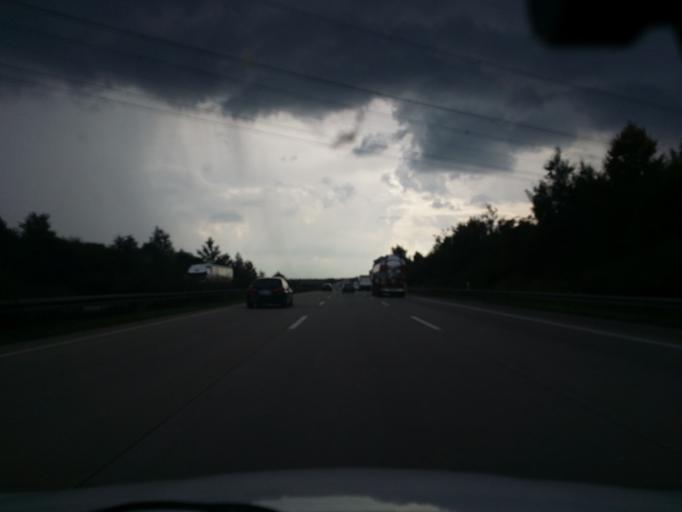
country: DE
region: Thuringia
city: Walpernhain
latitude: 51.0240
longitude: 11.9333
